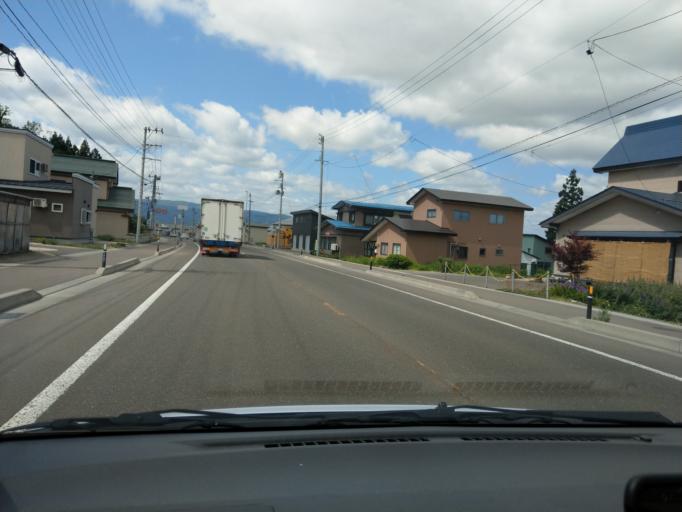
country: JP
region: Akita
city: Yuzawa
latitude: 39.1797
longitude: 140.4945
